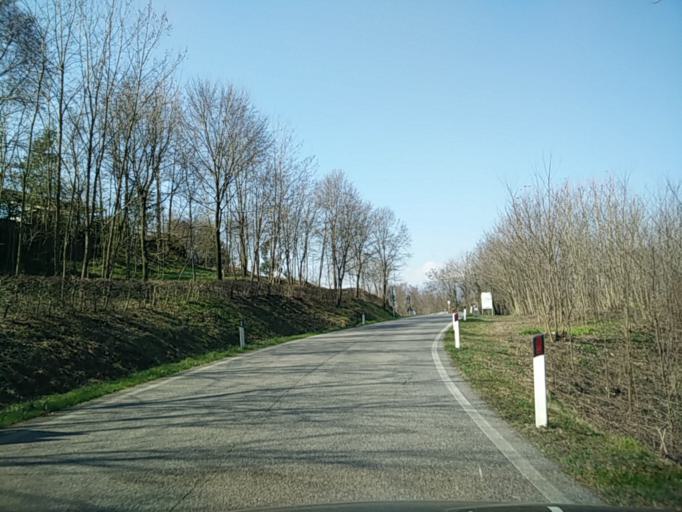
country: IT
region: Veneto
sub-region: Provincia di Treviso
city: Sernaglia della Battaglia
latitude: 45.8464
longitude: 12.1531
